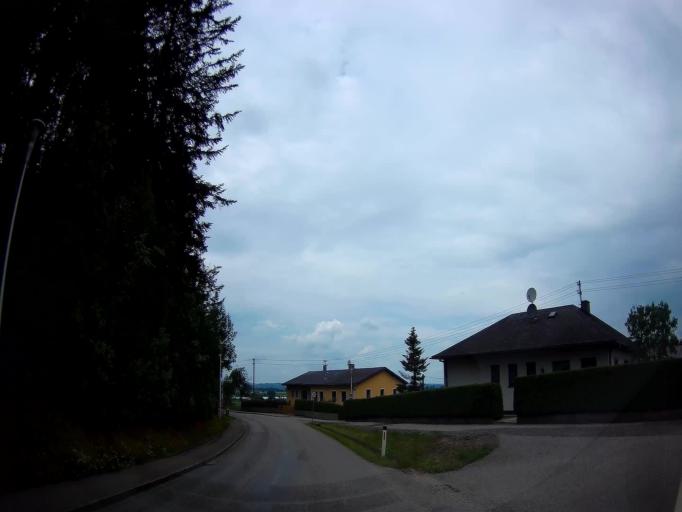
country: AT
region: Upper Austria
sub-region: Politischer Bezirk Braunau am Inn
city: Altheim
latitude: 48.2660
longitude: 13.3012
